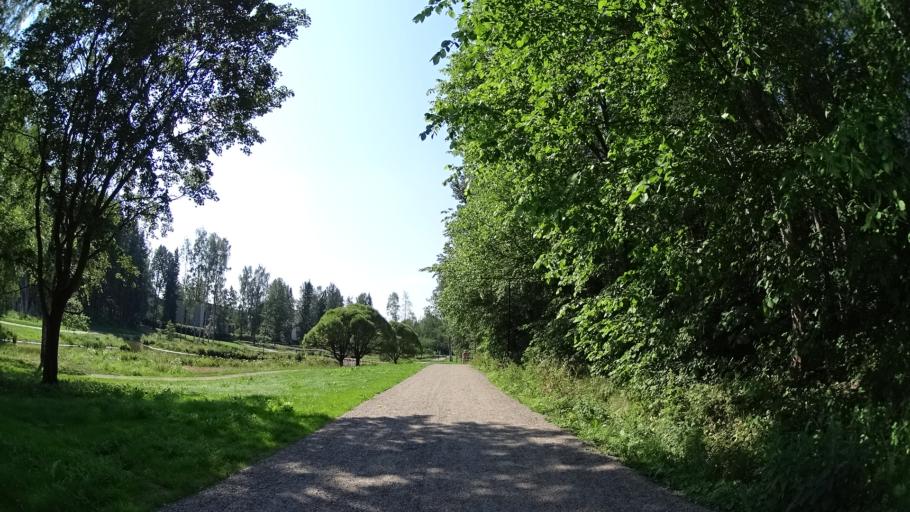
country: FI
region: Uusimaa
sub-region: Helsinki
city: Kerava
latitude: 60.3547
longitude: 25.0725
